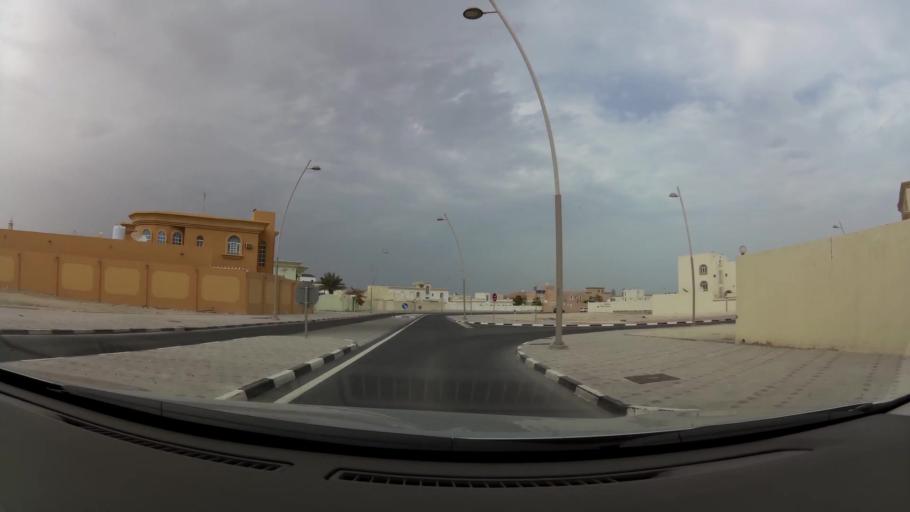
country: QA
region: Baladiyat ad Dawhah
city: Doha
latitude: 25.3449
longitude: 51.4930
